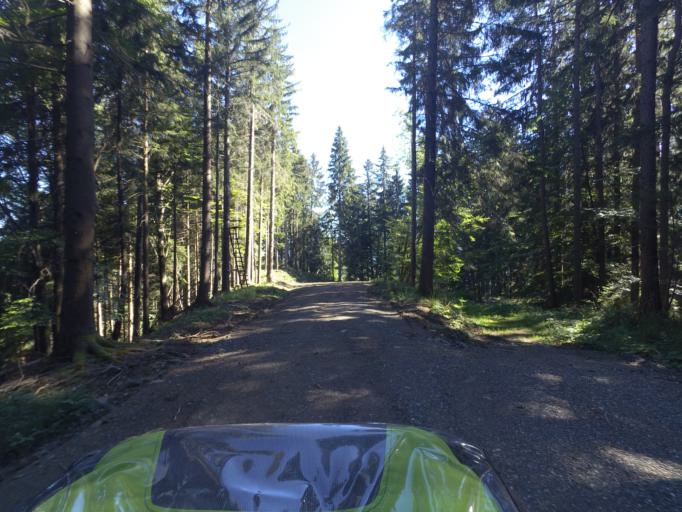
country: AT
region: Salzburg
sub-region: Politischer Bezirk Hallein
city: Hallein
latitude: 47.6558
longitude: 13.1043
